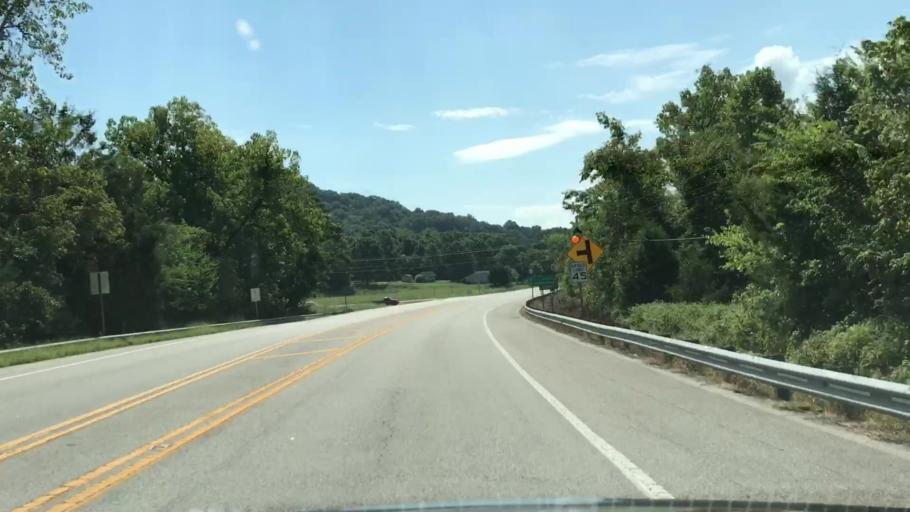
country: US
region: Tennessee
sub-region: Smith County
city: Carthage
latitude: 36.2889
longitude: -85.9928
